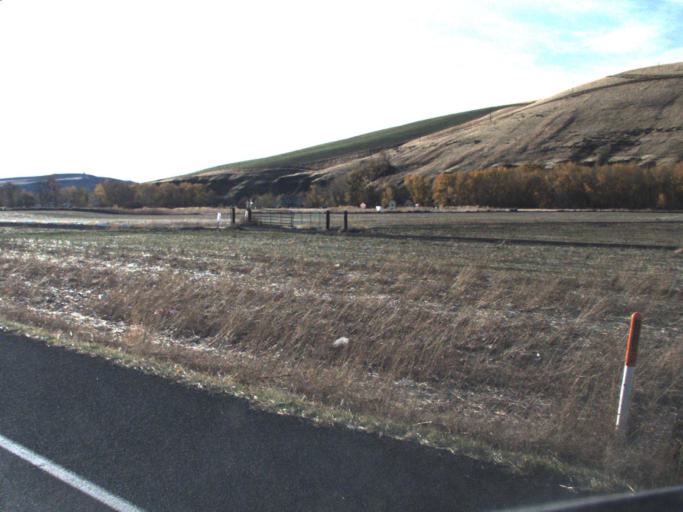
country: US
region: Washington
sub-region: Columbia County
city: Dayton
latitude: 46.2972
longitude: -118.0177
